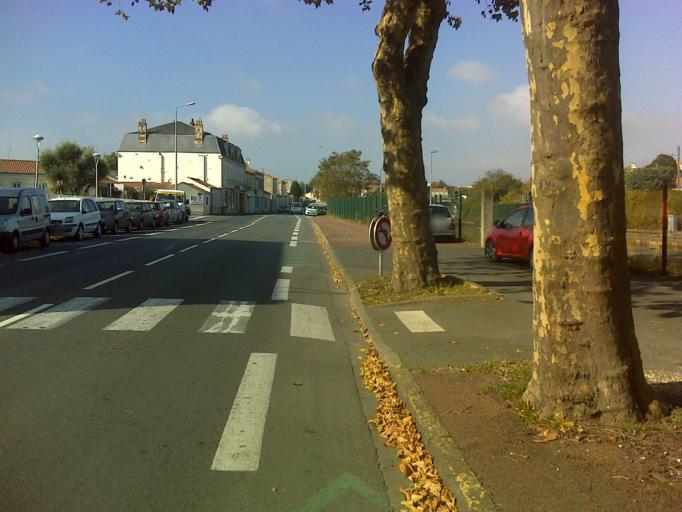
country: FR
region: Poitou-Charentes
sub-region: Departement de la Charente-Maritime
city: Rochefort
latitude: 45.9471
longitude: -0.9646
